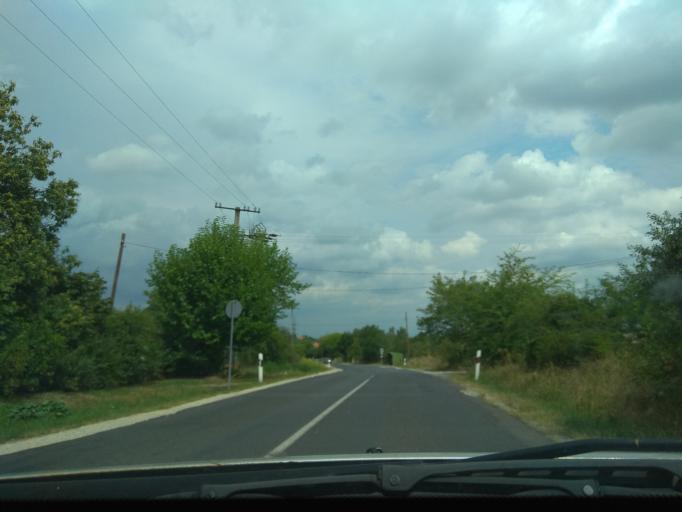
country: HU
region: Borsod-Abauj-Zemplen
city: Malyi
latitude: 48.0324
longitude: 20.7707
